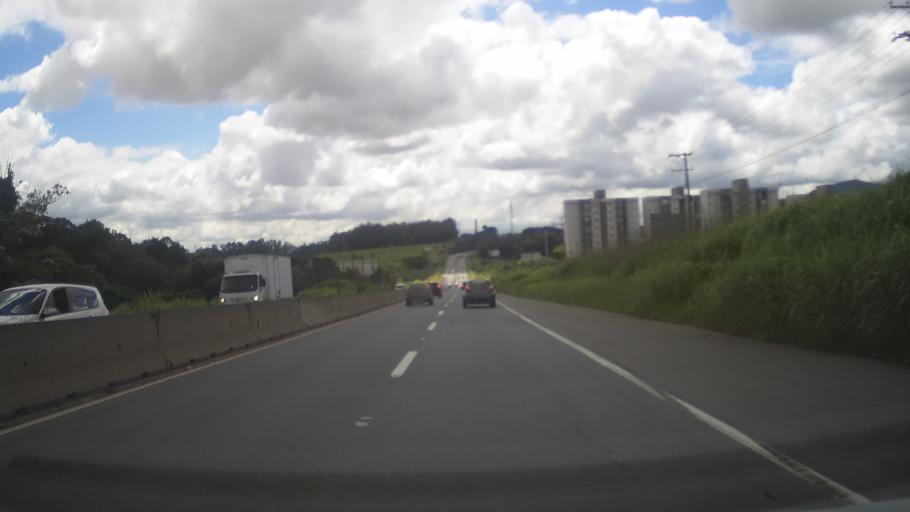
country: BR
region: Sao Paulo
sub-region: Itupeva
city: Itupeva
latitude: -23.1770
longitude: -46.9817
